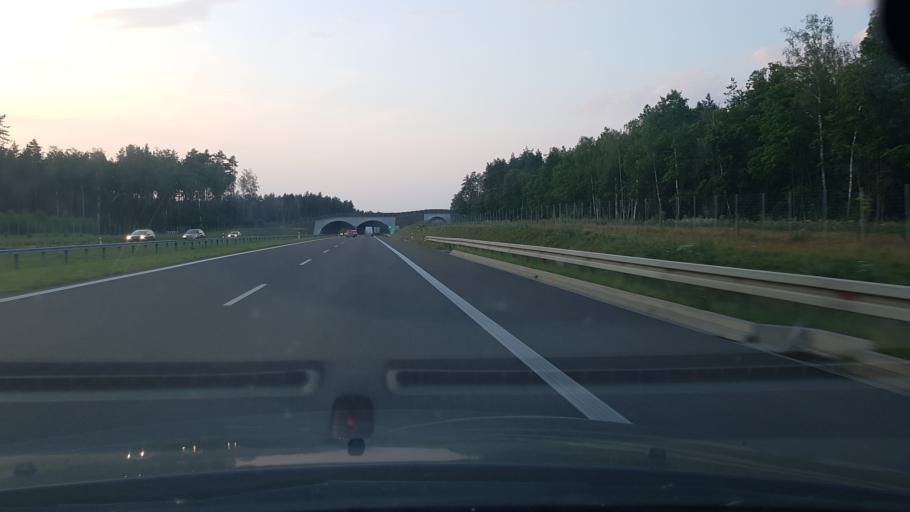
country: PL
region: Masovian Voivodeship
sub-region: Powiat mlawski
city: Wieczfnia Koscielna
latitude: 53.2484
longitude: 20.4244
